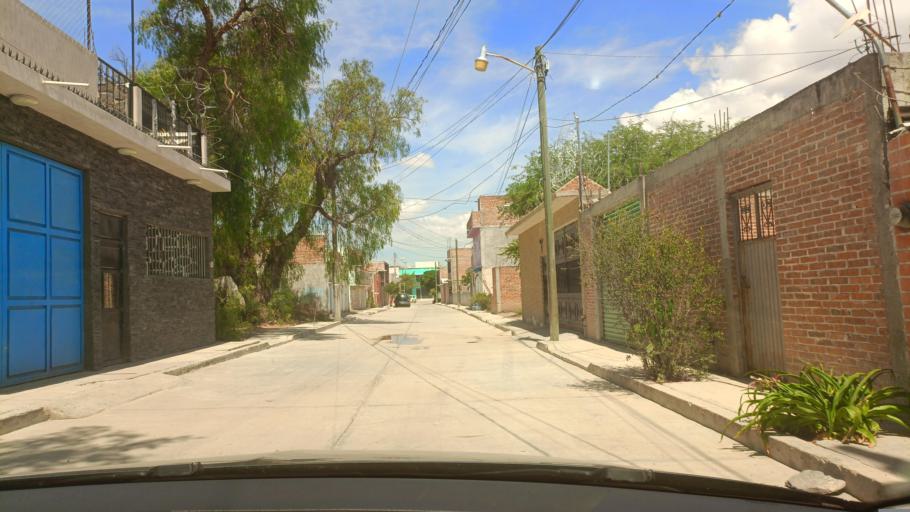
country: MX
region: Guanajuato
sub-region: San Luis de la Paz
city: San Luis de la Paz
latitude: 21.3036
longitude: -100.5055
